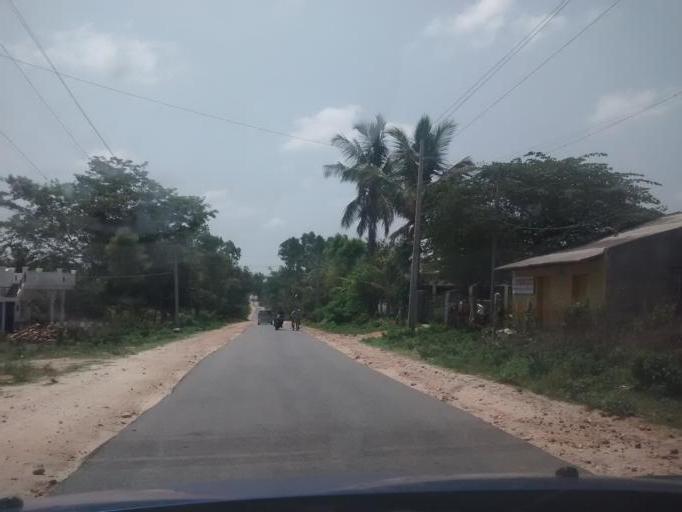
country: IN
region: Karnataka
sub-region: Mandya
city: Krishnarajpet
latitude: 12.5731
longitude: 76.2985
